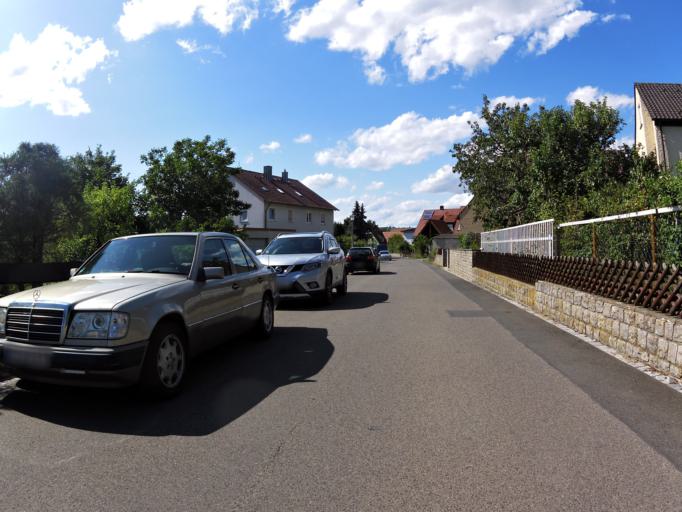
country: DE
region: Bavaria
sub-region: Regierungsbezirk Unterfranken
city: Marktsteft
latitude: 49.6935
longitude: 10.1396
